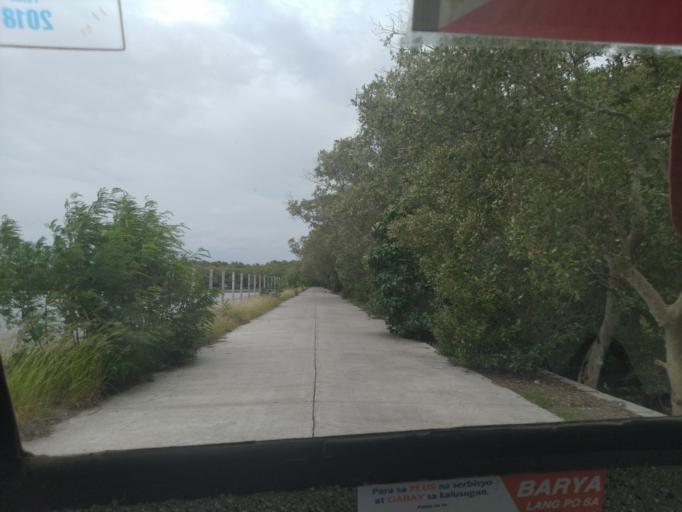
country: PH
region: Central Visayas
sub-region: Province of Negros Oriental
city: Okiot
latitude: 9.5444
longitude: 123.1534
